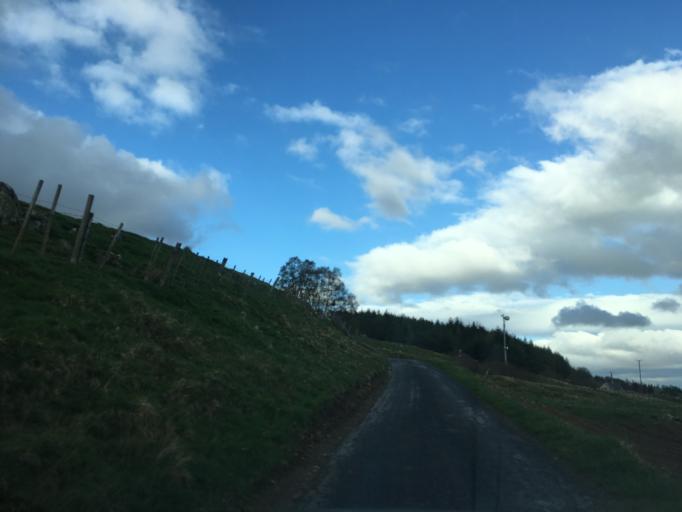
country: GB
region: Scotland
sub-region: Highland
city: Kingussie
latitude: 57.0211
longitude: -4.2987
